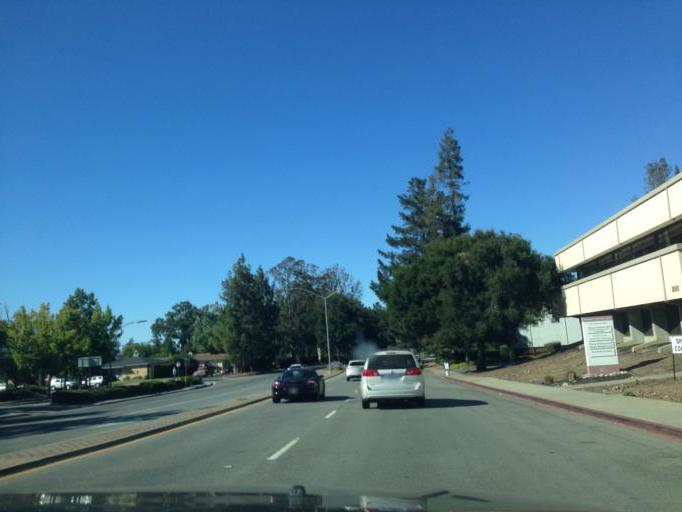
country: US
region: California
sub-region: San Mateo County
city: Woodside
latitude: 37.4492
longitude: -122.2312
